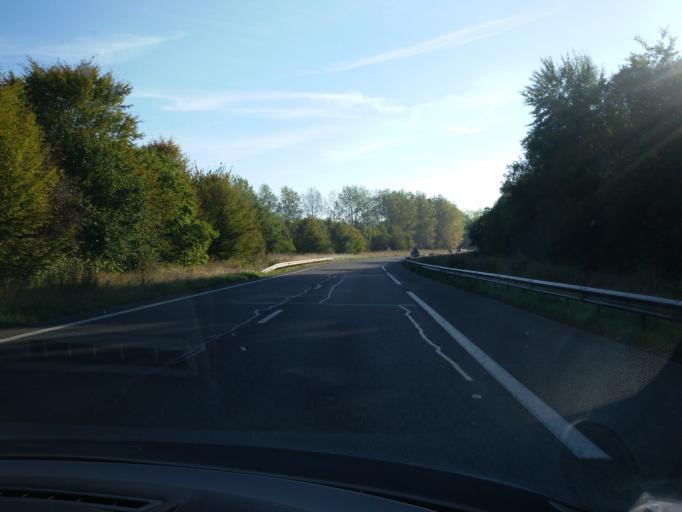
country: FR
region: Ile-de-France
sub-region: Departement de Seine-et-Marne
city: Bailly-Romainvilliers
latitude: 48.8374
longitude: 2.8153
